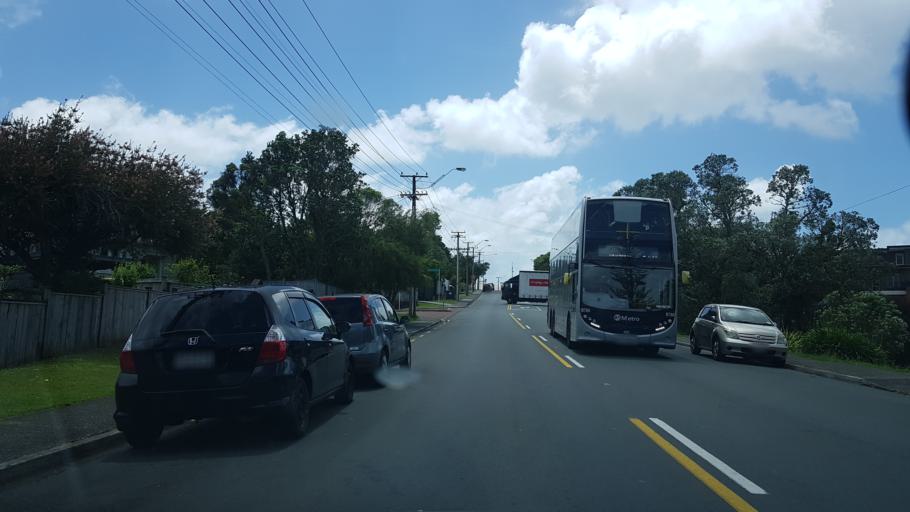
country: NZ
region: Auckland
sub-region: Auckland
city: North Shore
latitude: -36.8079
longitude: 174.7032
